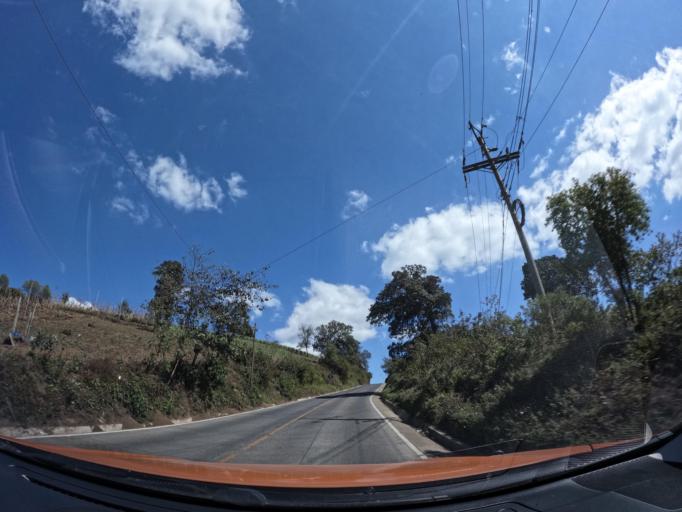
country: GT
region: Chimaltenango
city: Patzun
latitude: 14.6537
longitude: -91.0503
